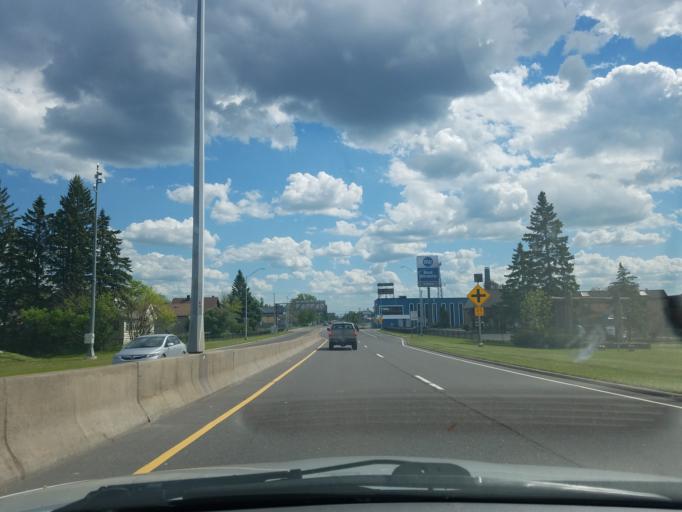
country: US
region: Wisconsin
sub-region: Douglas County
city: Superior
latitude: 46.7341
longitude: -92.0978
